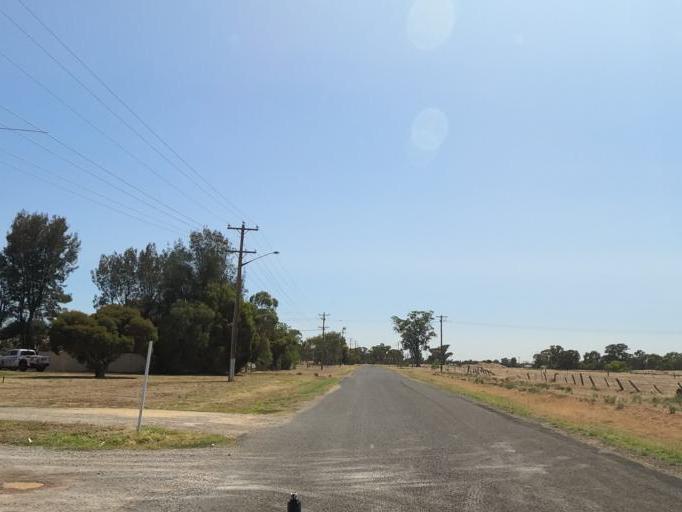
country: AU
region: New South Wales
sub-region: Corowa Shire
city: Mulwala
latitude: -35.9814
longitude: 146.0027
